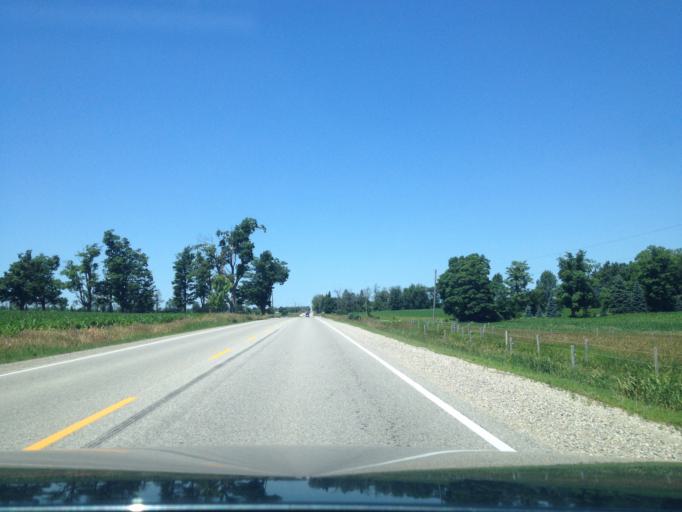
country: CA
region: Ontario
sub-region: Wellington County
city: Guelph
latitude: 43.6561
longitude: -80.2713
